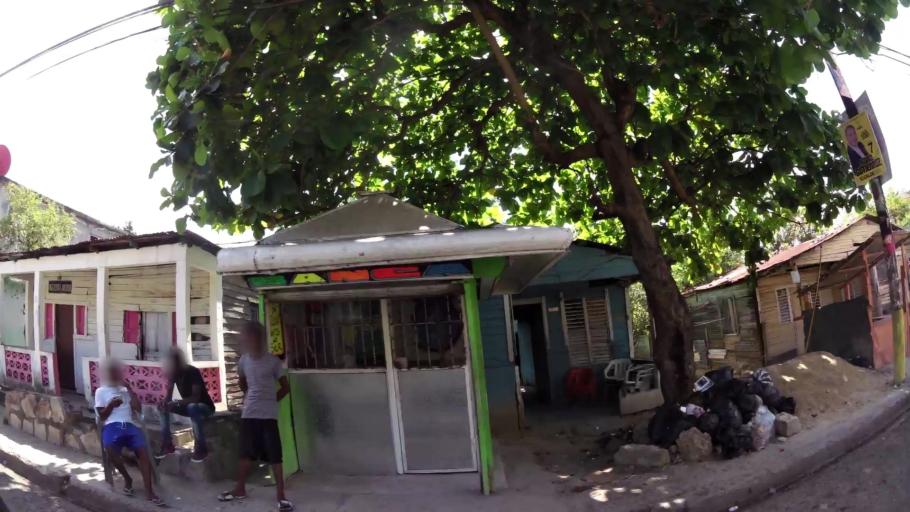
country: DO
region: San Cristobal
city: San Cristobal
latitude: 18.4239
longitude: -70.0829
